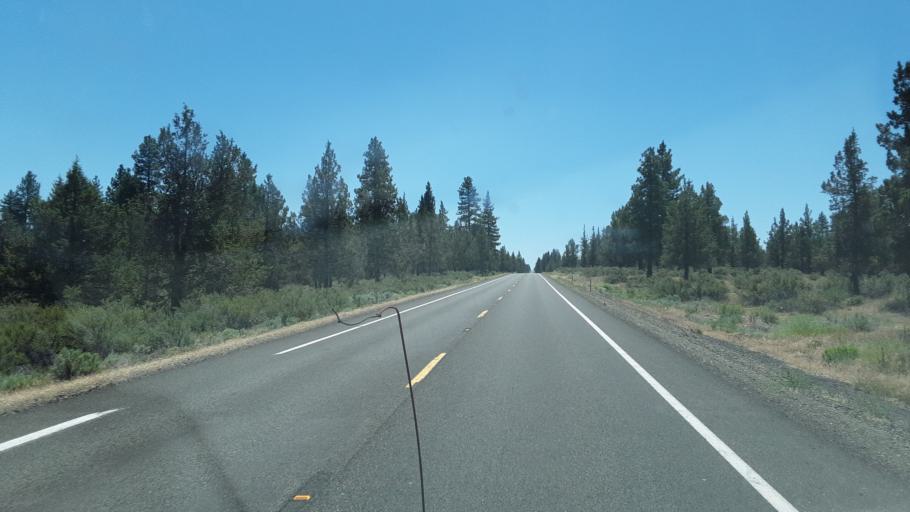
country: US
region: California
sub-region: Siskiyou County
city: Tulelake
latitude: 41.6338
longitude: -121.2299
